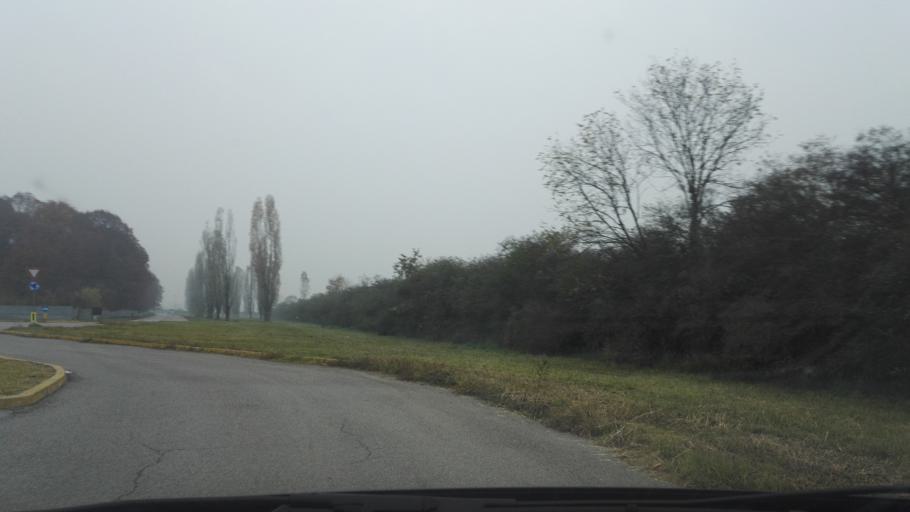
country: IT
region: Lombardy
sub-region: Citta metropolitana di Milano
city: Novegro-Tregarezzo-San Felice
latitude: 45.4704
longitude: 9.2971
